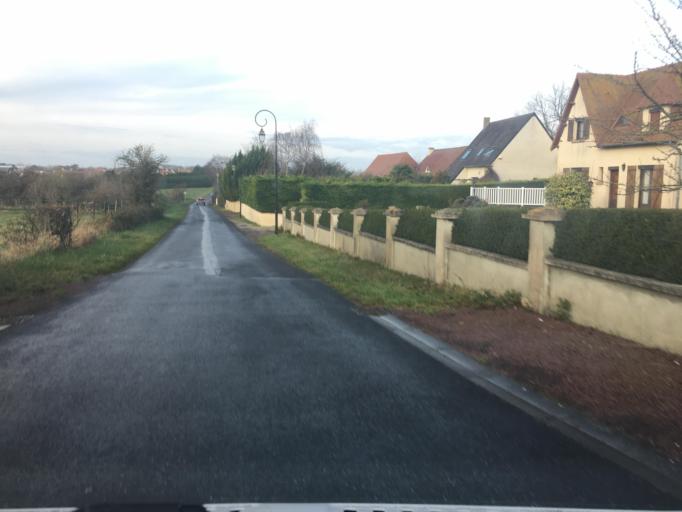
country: FR
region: Lower Normandy
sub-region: Departement du Calvados
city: Rots
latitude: 49.2043
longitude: -0.4656
